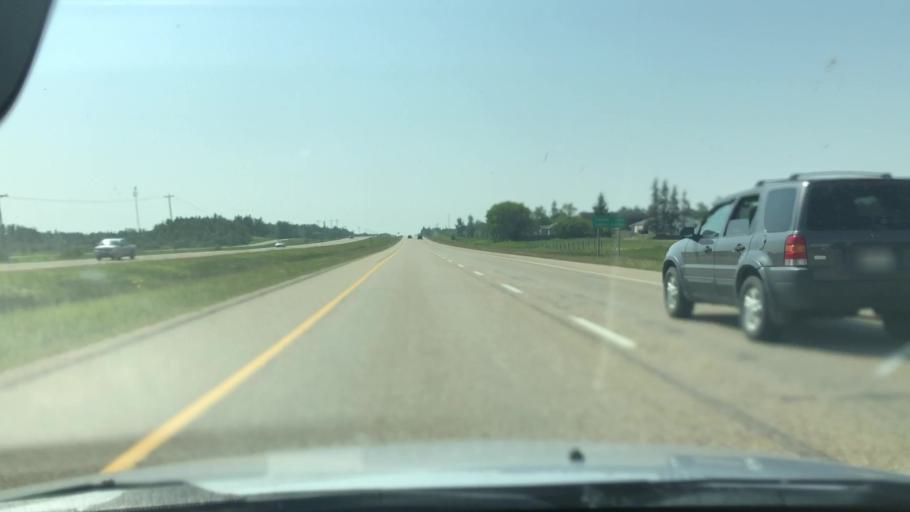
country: CA
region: Alberta
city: Devon
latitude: 53.4459
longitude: -113.7635
